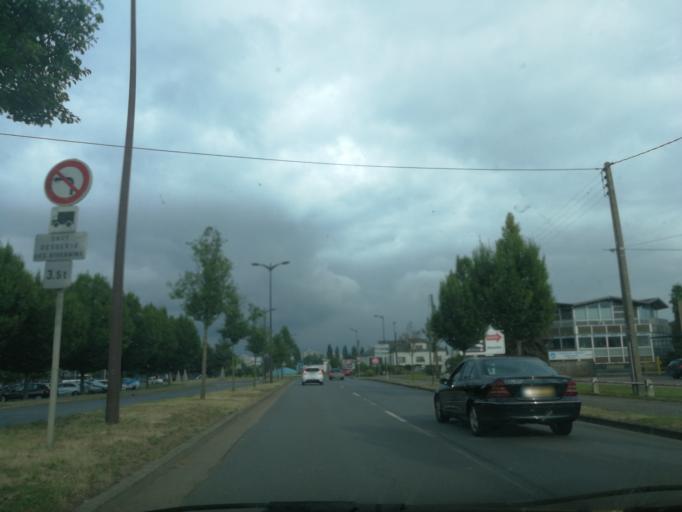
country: FR
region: Lorraine
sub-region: Departement de la Moselle
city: Terville
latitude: 49.3579
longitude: 6.1354
